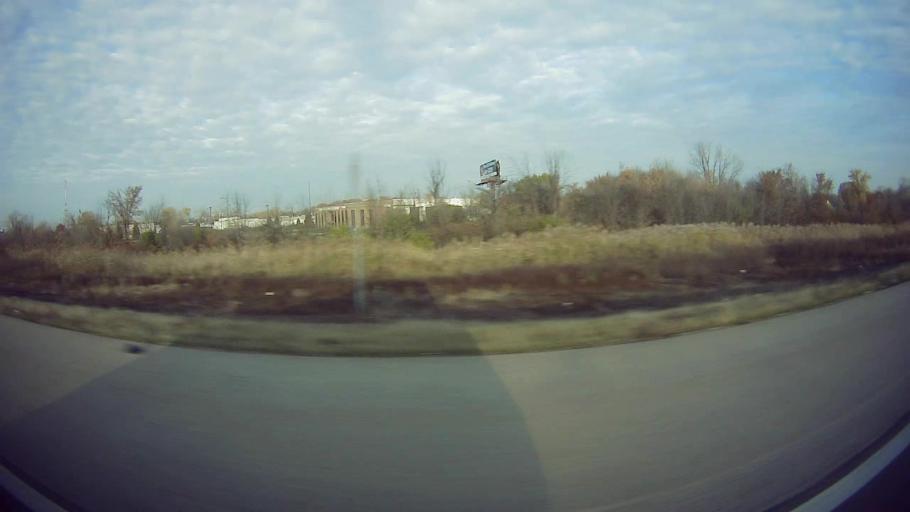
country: US
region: Michigan
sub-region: Macomb County
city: Saint Clair Shores
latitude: 42.5418
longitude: -82.8841
